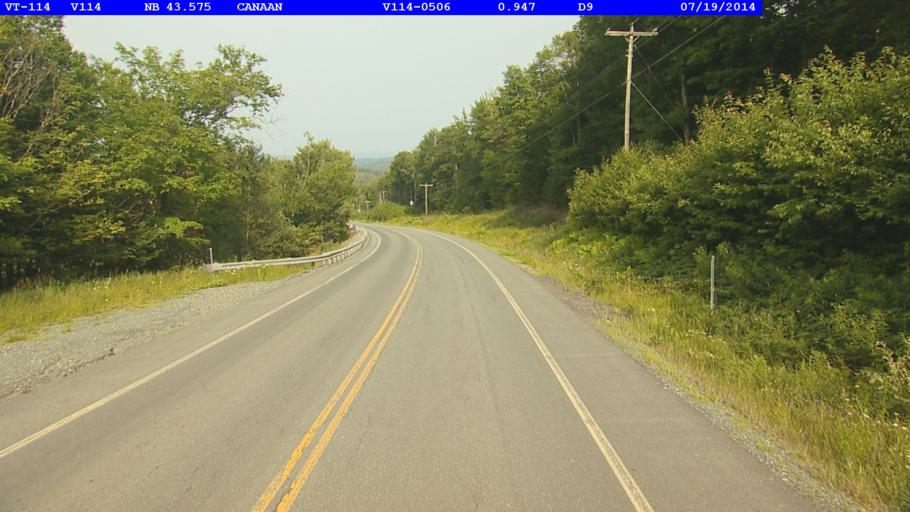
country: CA
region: Quebec
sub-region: Estrie
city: Coaticook
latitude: 45.0058
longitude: -71.6745
